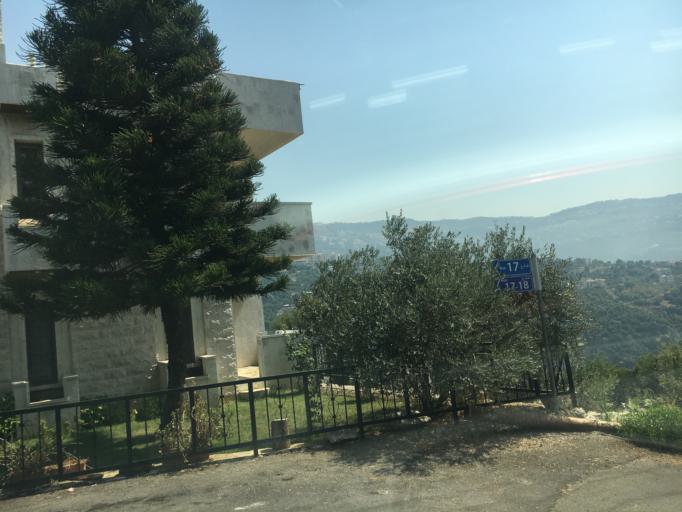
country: LB
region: Mont-Liban
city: Djounie
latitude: 33.9526
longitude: 35.6973
